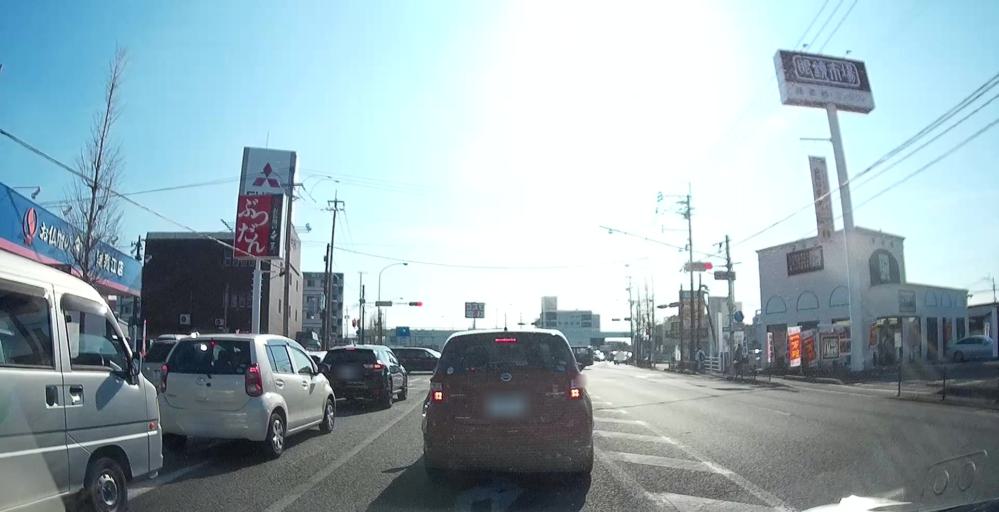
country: JP
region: Kumamoto
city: Kumamoto
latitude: 32.7534
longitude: 130.6871
